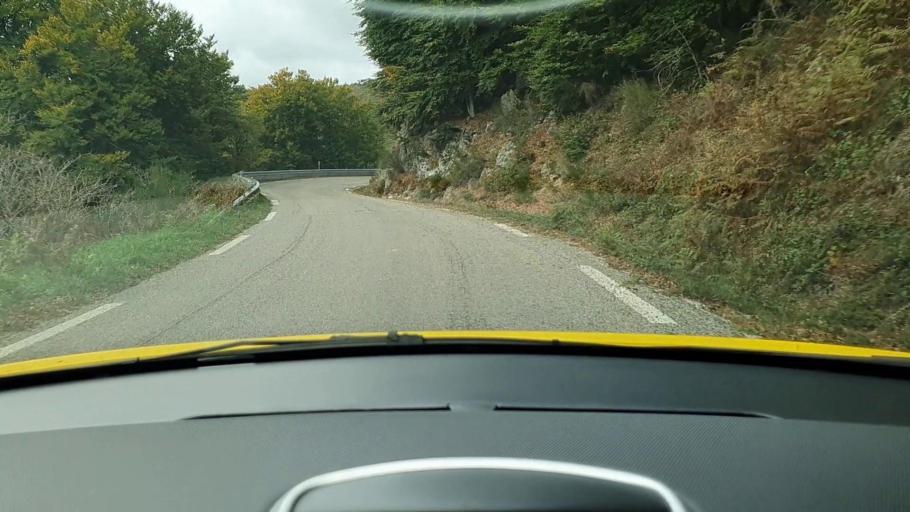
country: FR
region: Languedoc-Roussillon
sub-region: Departement du Gard
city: Le Vigan
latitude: 44.0455
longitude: 3.5566
